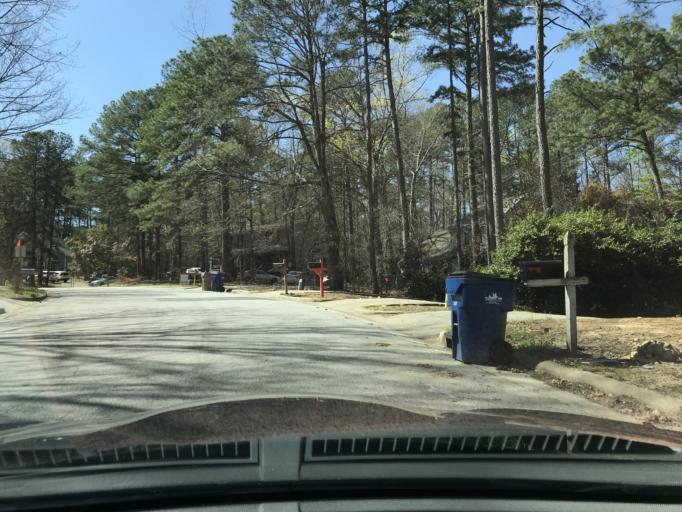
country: US
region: North Carolina
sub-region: Wake County
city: West Raleigh
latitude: 35.7740
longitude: -78.6957
